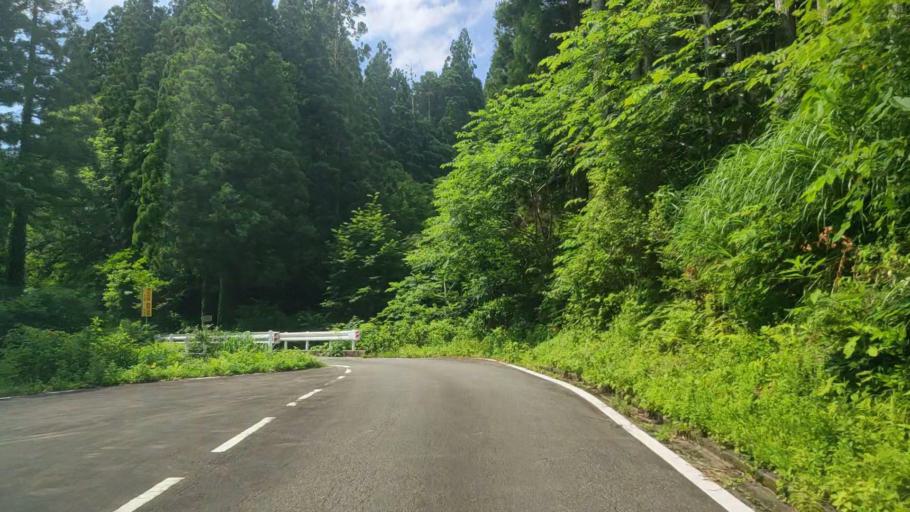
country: JP
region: Fukui
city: Katsuyama
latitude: 36.1769
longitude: 136.5216
